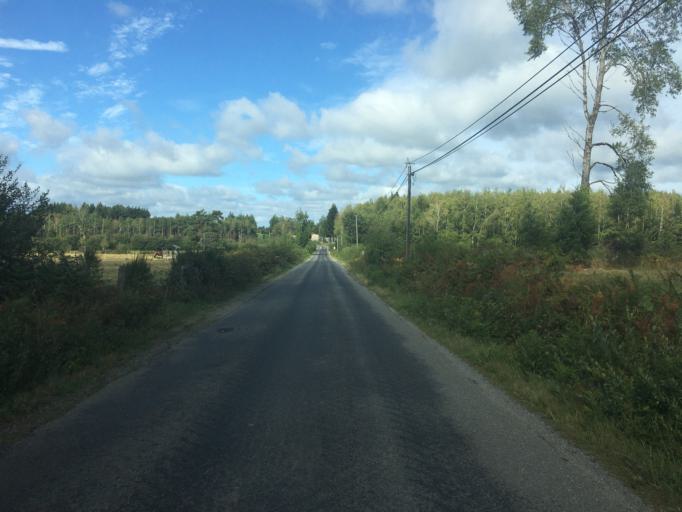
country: FR
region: Auvergne
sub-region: Departement du Cantal
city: Champagnac
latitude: 45.4160
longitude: 2.4189
